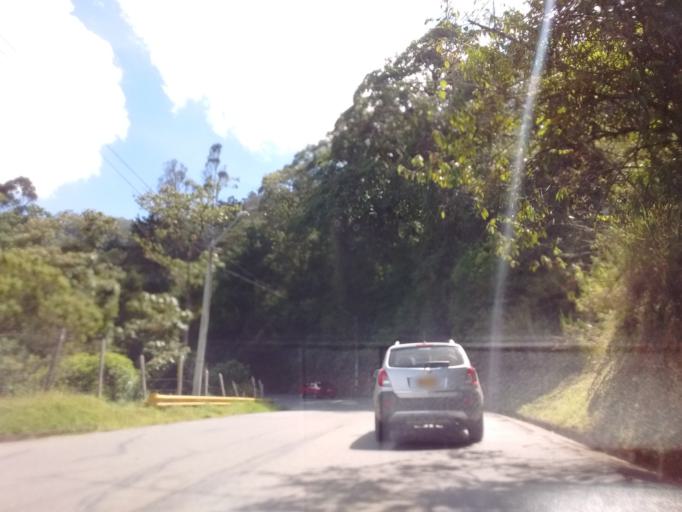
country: CO
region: Antioquia
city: Medellin
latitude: 6.2391
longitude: -75.5131
